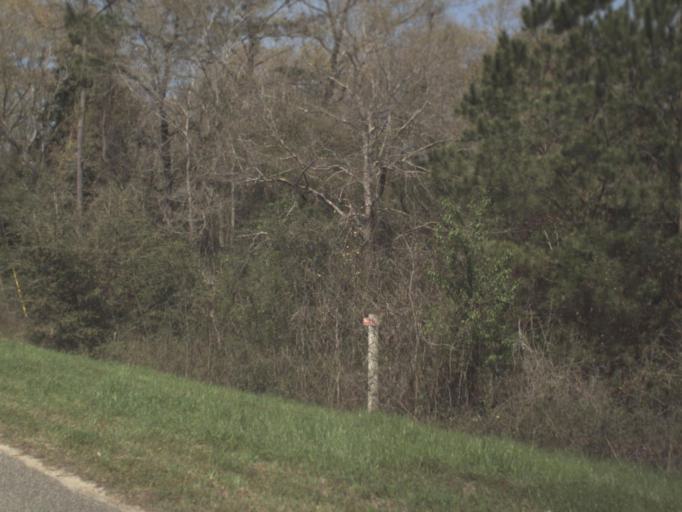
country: US
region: Florida
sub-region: Liberty County
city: Bristol
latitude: 30.4321
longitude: -84.9478
